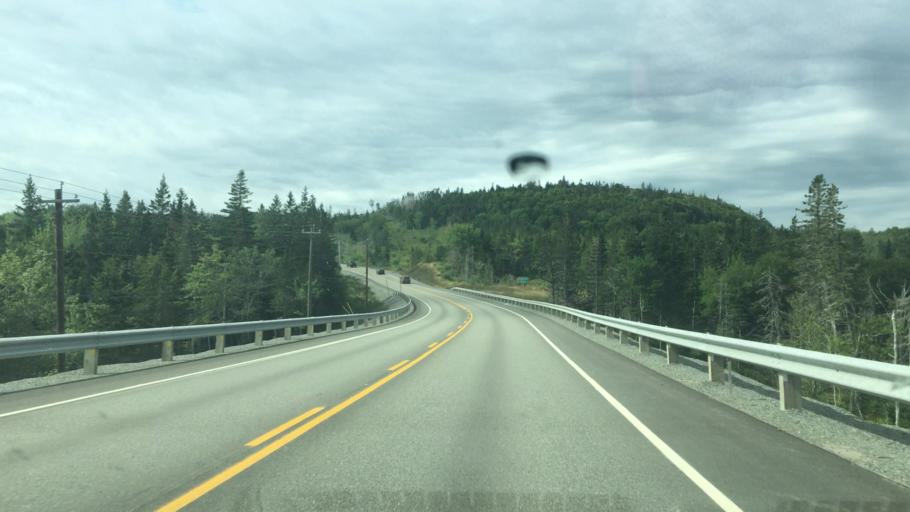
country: CA
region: Nova Scotia
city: Princeville
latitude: 45.6669
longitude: -60.8098
